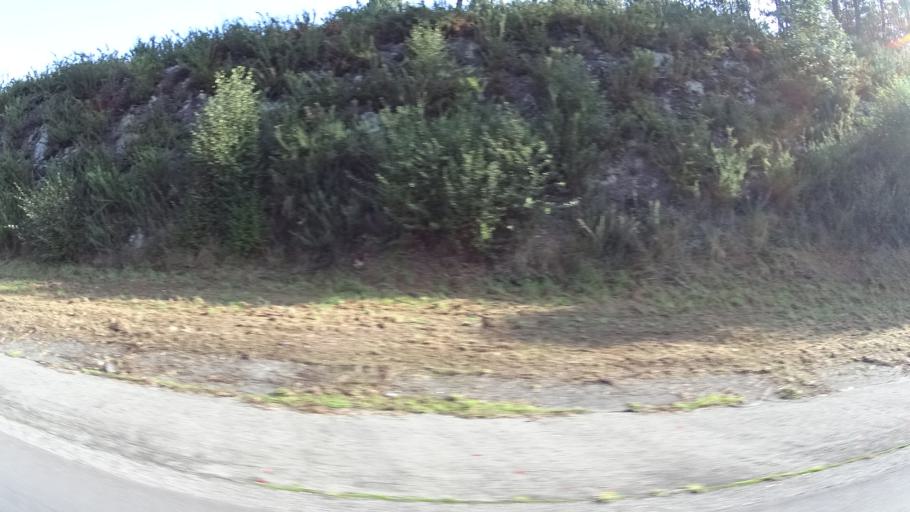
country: ES
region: Galicia
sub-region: Provincia da Coruna
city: Aranga
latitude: 43.2256
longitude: -8.0610
